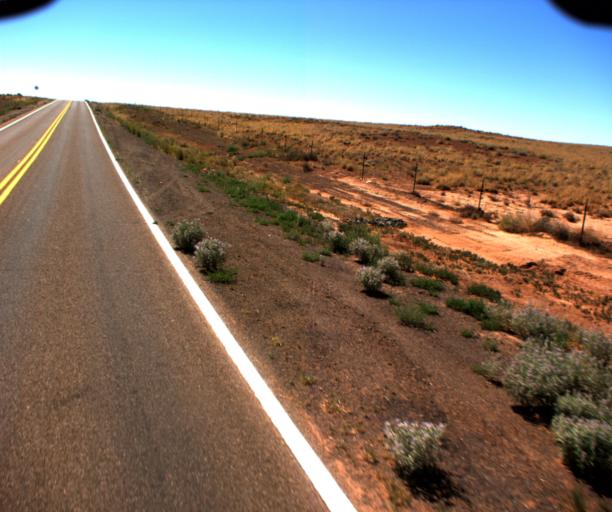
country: US
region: Arizona
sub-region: Navajo County
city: Winslow
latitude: 35.0046
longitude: -110.6903
